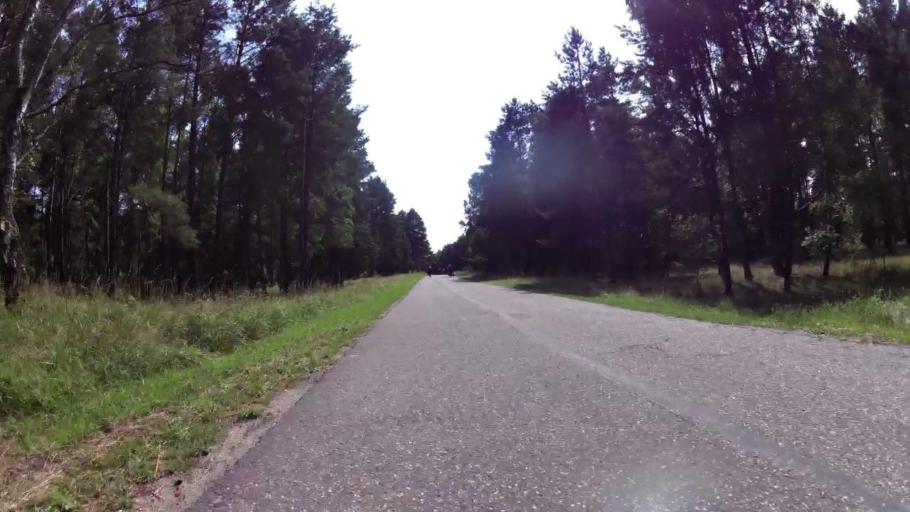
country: PL
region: West Pomeranian Voivodeship
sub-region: Powiat choszczenski
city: Drawno
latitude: 53.3224
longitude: 15.6893
